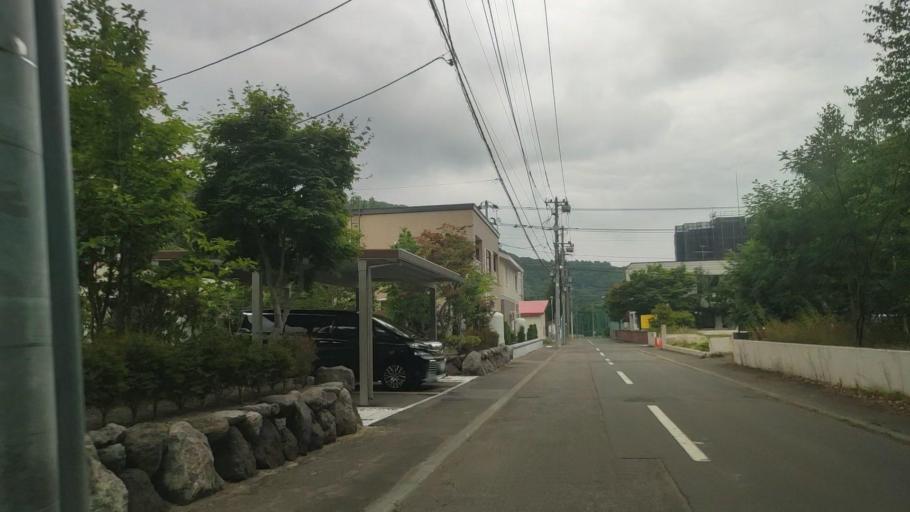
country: JP
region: Hokkaido
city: Sapporo
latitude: 42.9718
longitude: 141.1696
